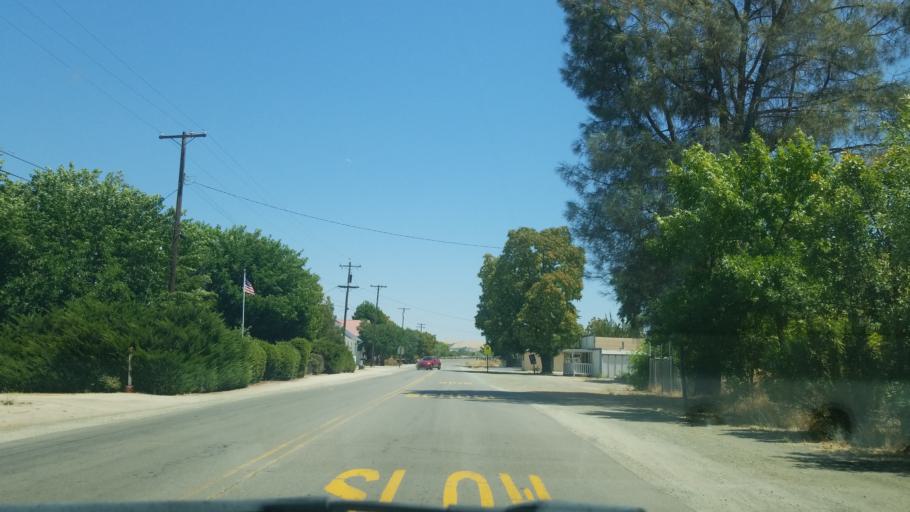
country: US
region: California
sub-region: San Luis Obispo County
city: Atascadero
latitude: 35.5192
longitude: -120.5239
